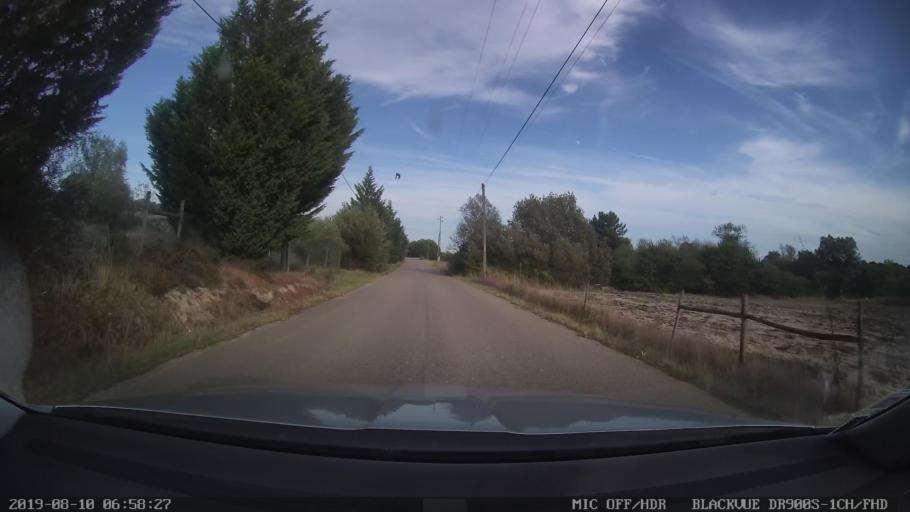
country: PT
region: Santarem
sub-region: Benavente
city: Poceirao
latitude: 38.8484
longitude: -8.7159
